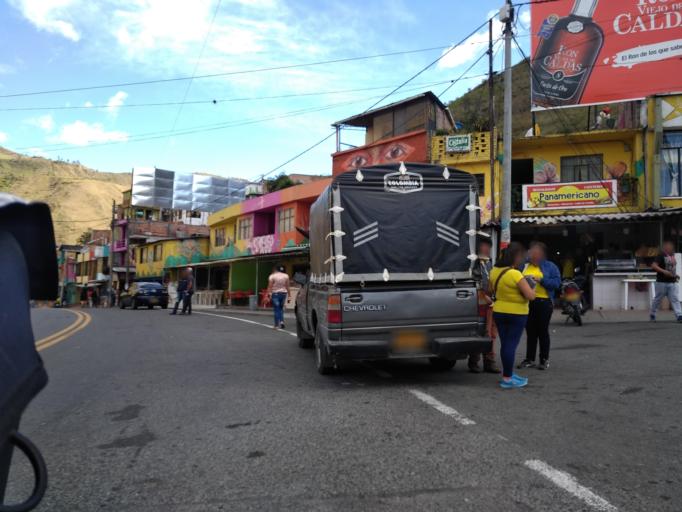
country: CO
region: Narino
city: Funes
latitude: 1.0499
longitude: -77.4530
